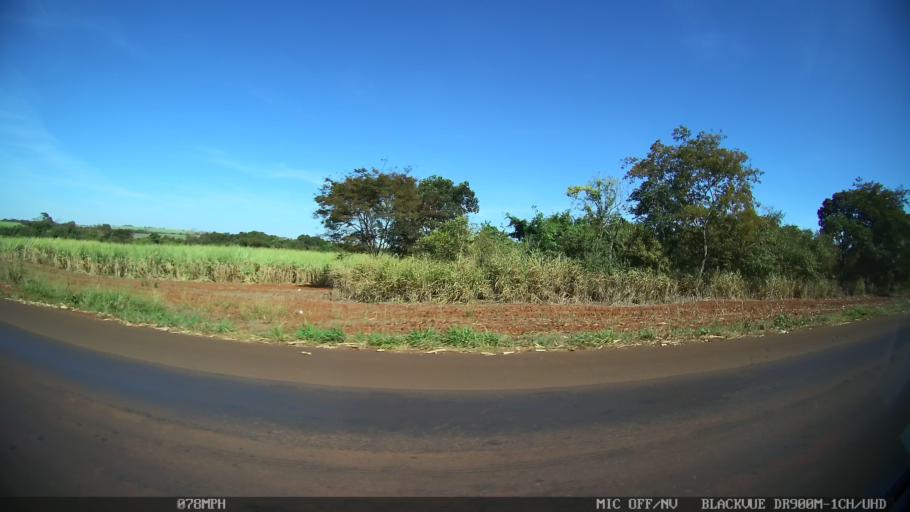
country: BR
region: Sao Paulo
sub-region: Ipua
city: Ipua
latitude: -20.5004
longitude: -47.9533
